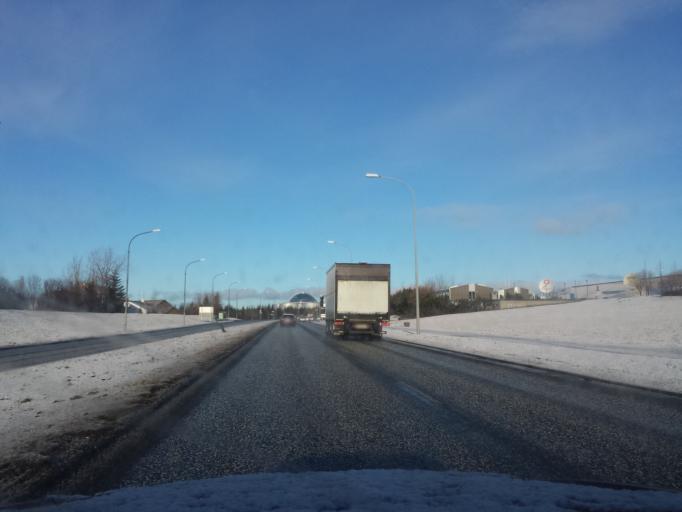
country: IS
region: Capital Region
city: Reykjavik
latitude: 64.1266
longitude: -21.9035
